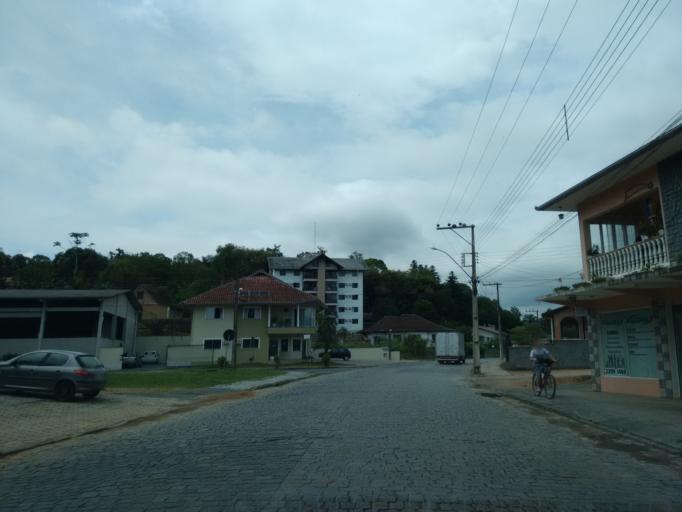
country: BR
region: Santa Catarina
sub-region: Pomerode
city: Pomerode
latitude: -26.7291
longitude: -49.1713
